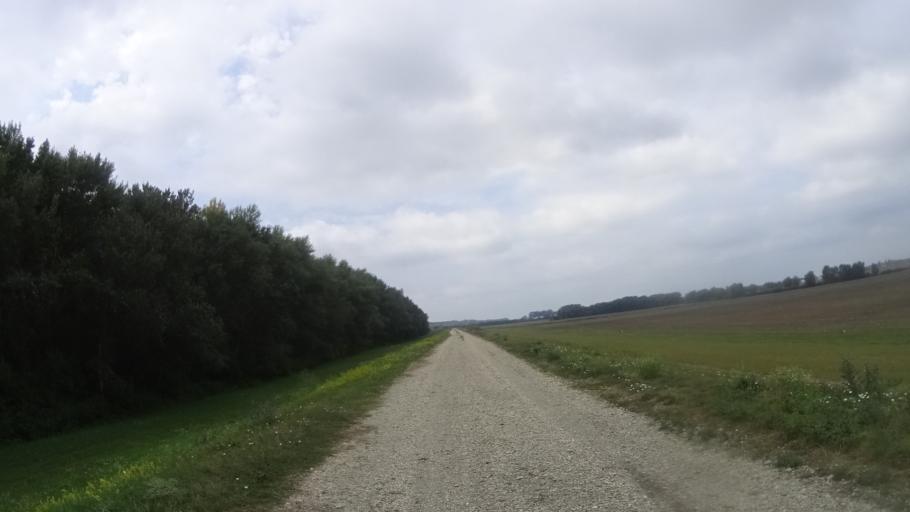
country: HU
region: Gyor-Moson-Sopron
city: Bony
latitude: 47.7475
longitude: 17.9067
